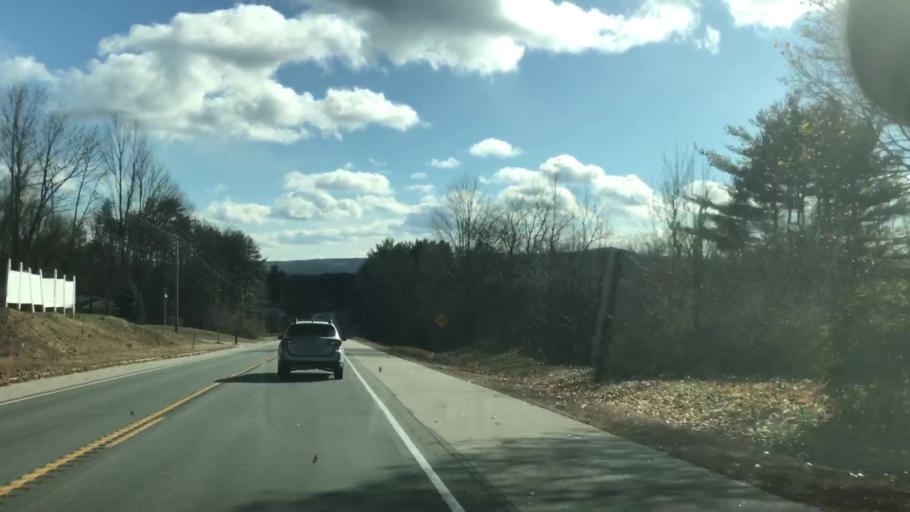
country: US
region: New Hampshire
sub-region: Strafford County
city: New Durham
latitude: 43.4610
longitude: -71.2206
